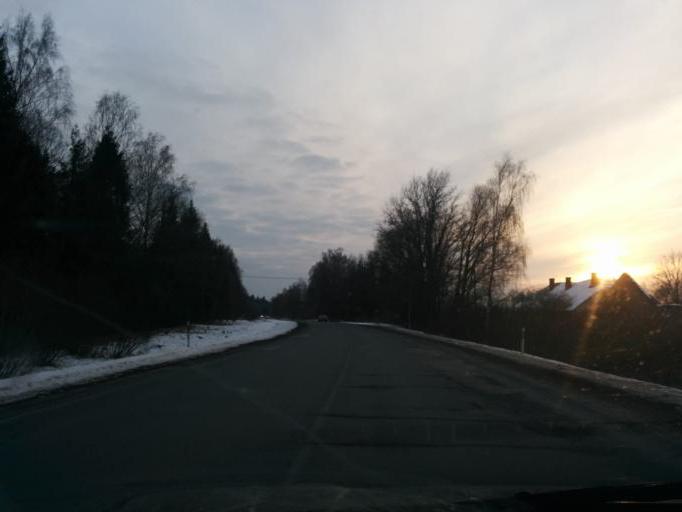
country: LV
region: Amatas Novads
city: Drabesi
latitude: 57.2521
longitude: 25.3385
